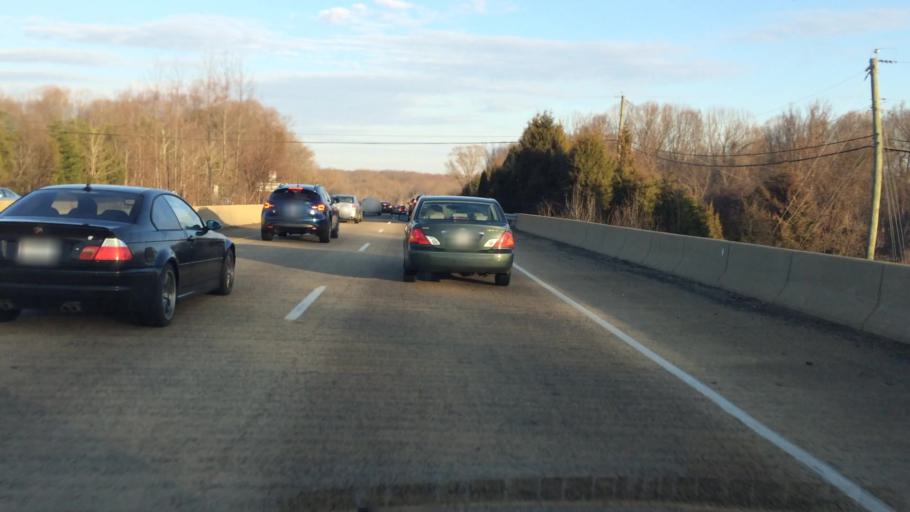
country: US
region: Virginia
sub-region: Fairfax County
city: Fairfax Station
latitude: 38.7991
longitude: -77.3394
